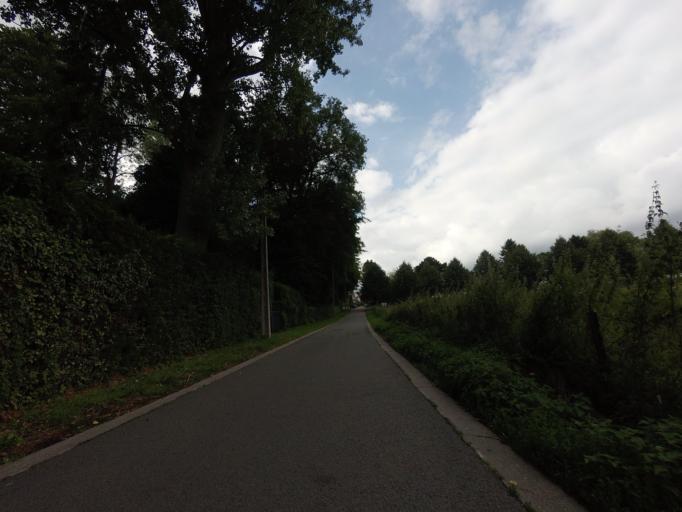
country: BE
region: Flanders
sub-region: Provincie Vlaams-Brabant
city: Meise
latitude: 50.9318
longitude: 4.3413
